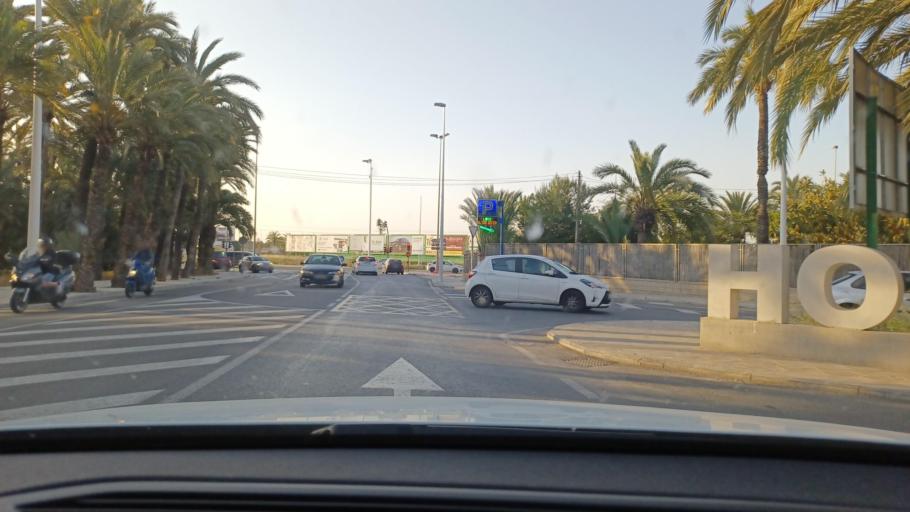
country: ES
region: Valencia
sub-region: Provincia de Alicante
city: Elche
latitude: 38.2596
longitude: -0.6835
